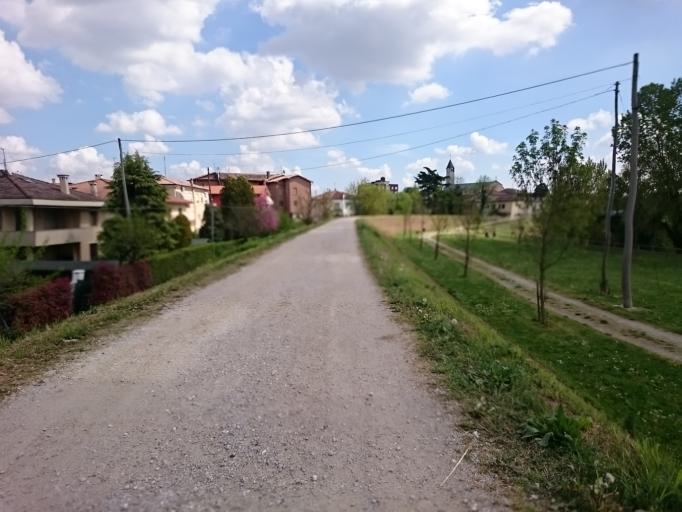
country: IT
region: Veneto
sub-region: Provincia di Padova
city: Tencarola
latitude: 45.3923
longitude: 11.8064
